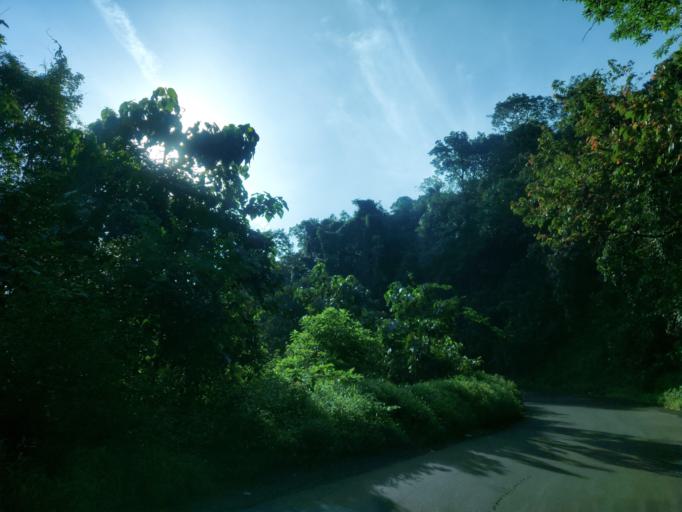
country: IN
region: Maharashtra
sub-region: Sindhudurg
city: Savantvadi
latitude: 15.9364
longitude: 73.9726
